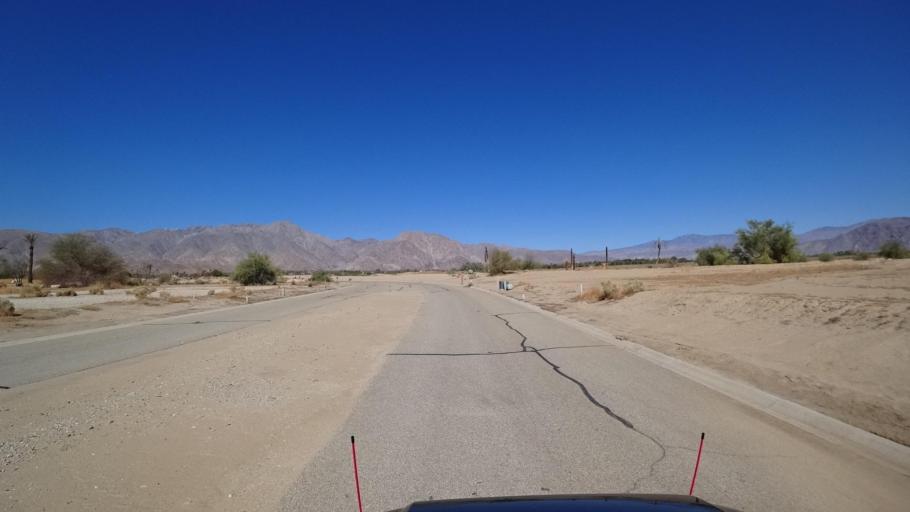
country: US
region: California
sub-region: San Diego County
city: Borrego Springs
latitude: 33.2478
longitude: -116.3535
